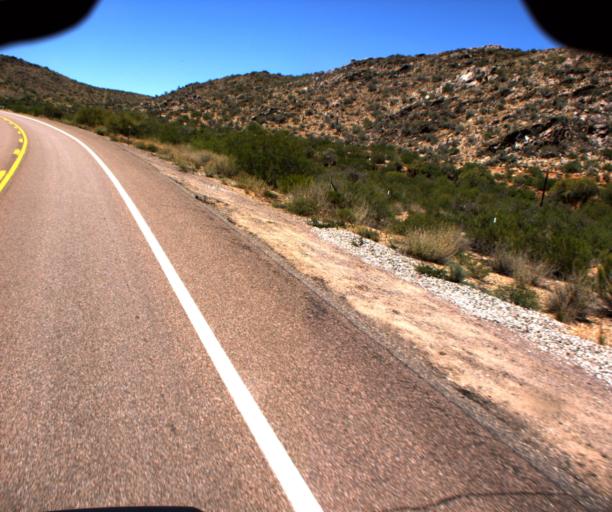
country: US
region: Arizona
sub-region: Yavapai County
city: Bagdad
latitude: 34.5309
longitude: -113.1384
